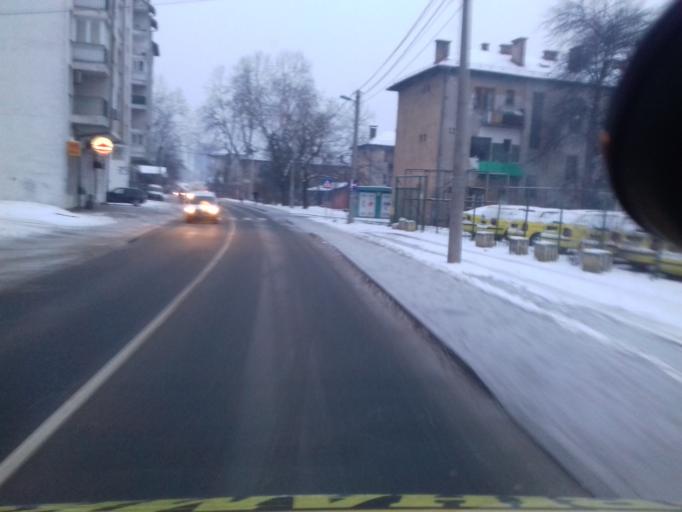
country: BA
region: Federation of Bosnia and Herzegovina
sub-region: Kanton Sarajevo
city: Sarajevo
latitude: 43.8569
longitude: 18.3658
